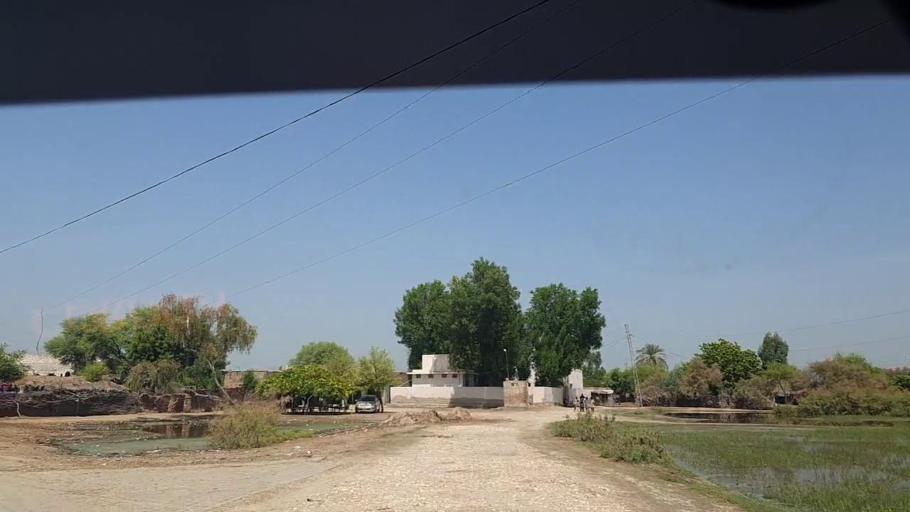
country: PK
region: Sindh
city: Ghauspur
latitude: 28.1880
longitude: 69.0884
